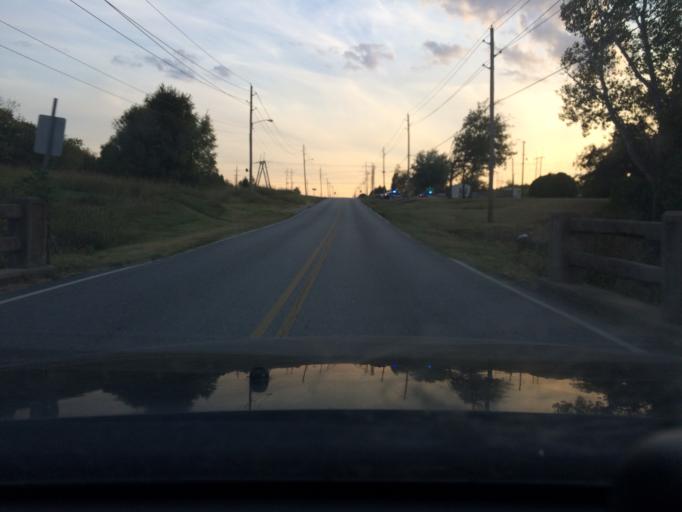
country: US
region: Oklahoma
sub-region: Rogers County
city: Catoosa
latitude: 36.1757
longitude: -95.7534
